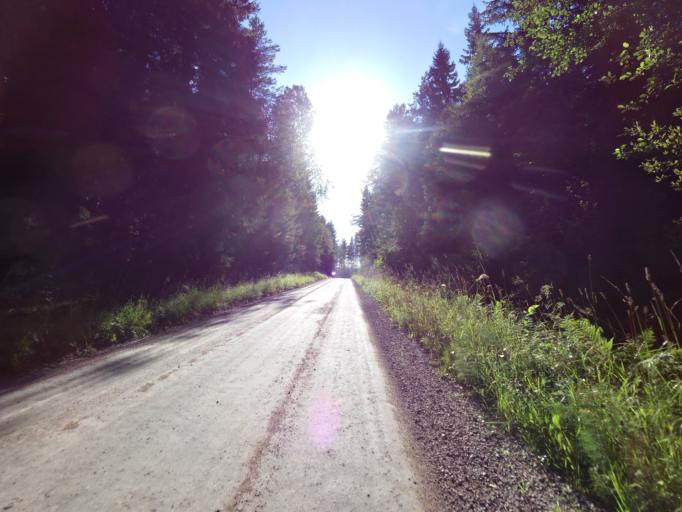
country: SE
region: Gaevleborg
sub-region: Hofors Kommun
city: Hofors
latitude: 60.5679
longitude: 16.2545
